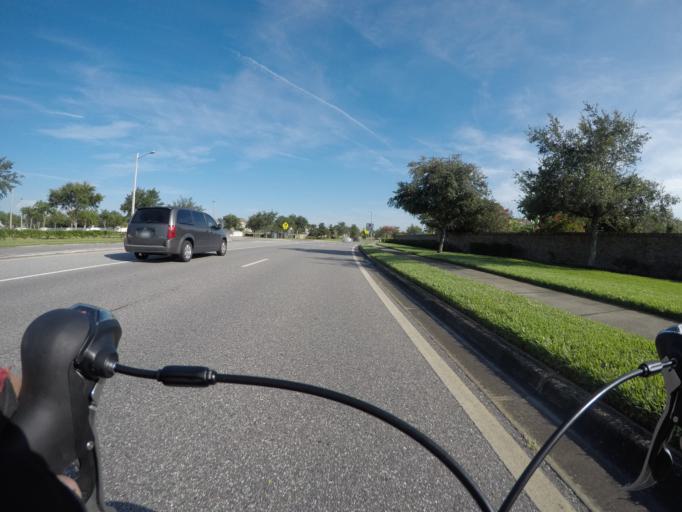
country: US
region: Florida
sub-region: Osceola County
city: Buenaventura Lakes
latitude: 28.3560
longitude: -81.3480
